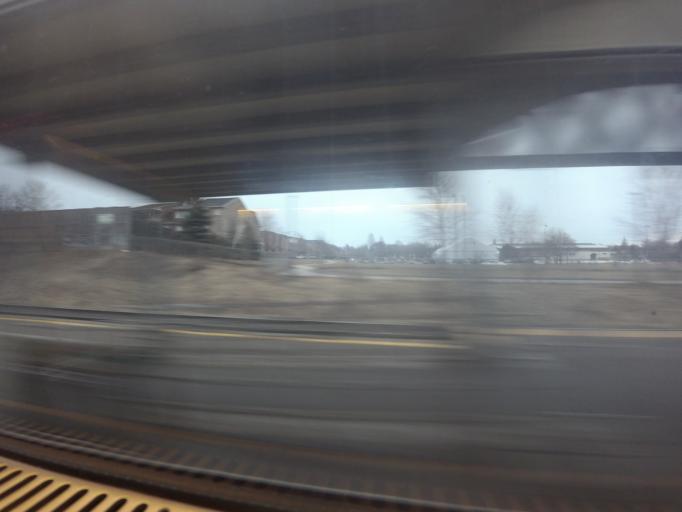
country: CA
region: Ontario
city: Scarborough
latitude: 43.6867
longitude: -79.2987
